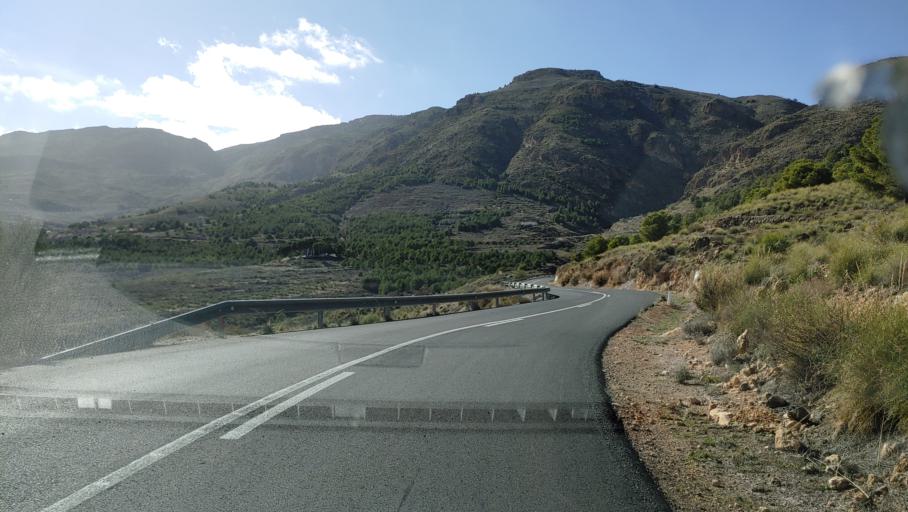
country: ES
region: Andalusia
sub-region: Provincia de Almeria
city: Alicun
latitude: 36.9470
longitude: -2.5973
